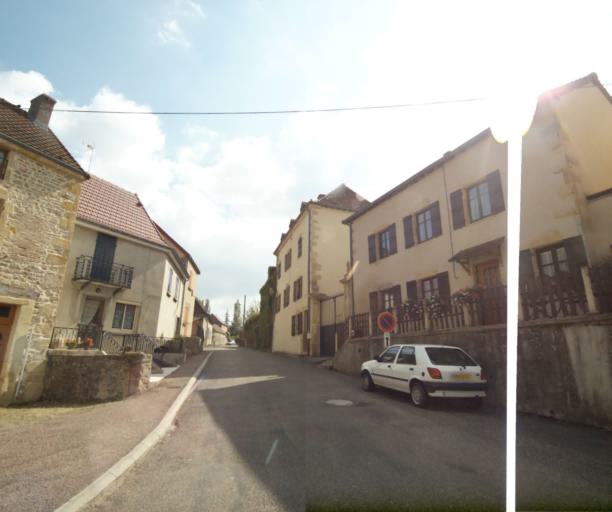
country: FR
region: Bourgogne
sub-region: Departement de Saone-et-Loire
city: Charolles
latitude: 46.3653
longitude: 4.2326
